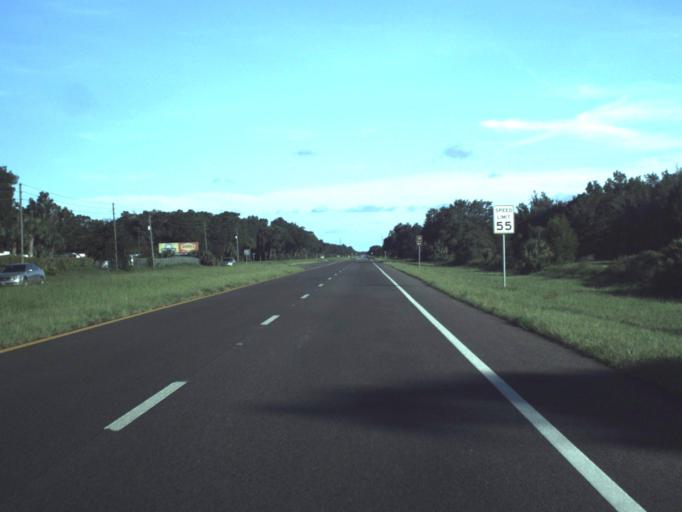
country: US
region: Florida
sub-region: Levy County
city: Inglis
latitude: 29.0052
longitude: -82.6585
